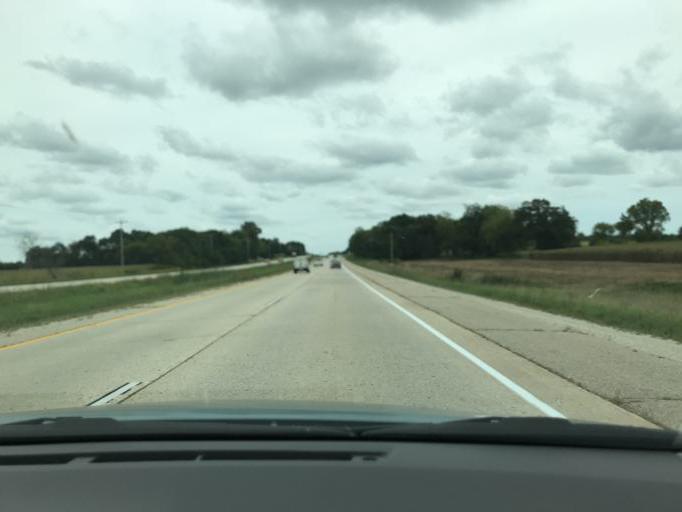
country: US
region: Wisconsin
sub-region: Kenosha County
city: Paddock Lake
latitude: 42.5680
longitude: -88.0838
